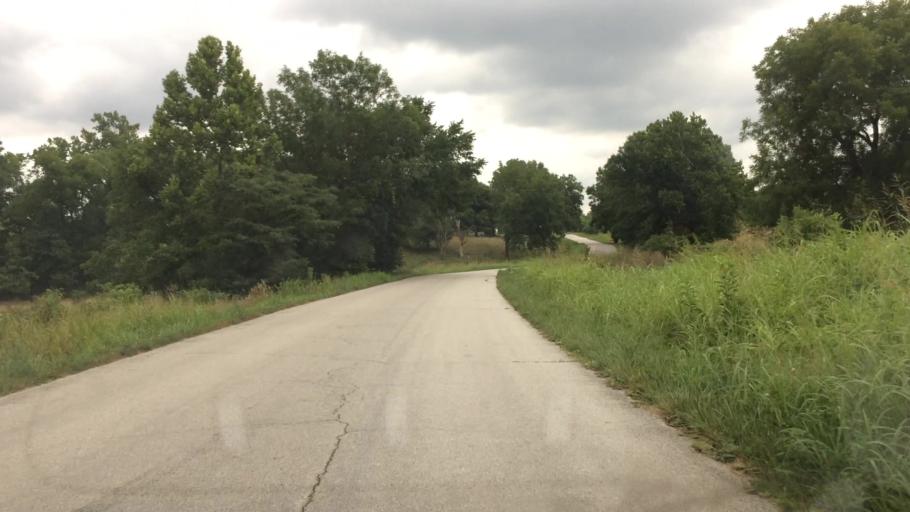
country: US
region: Missouri
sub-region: Greene County
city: Strafford
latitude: 37.3134
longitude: -93.0696
